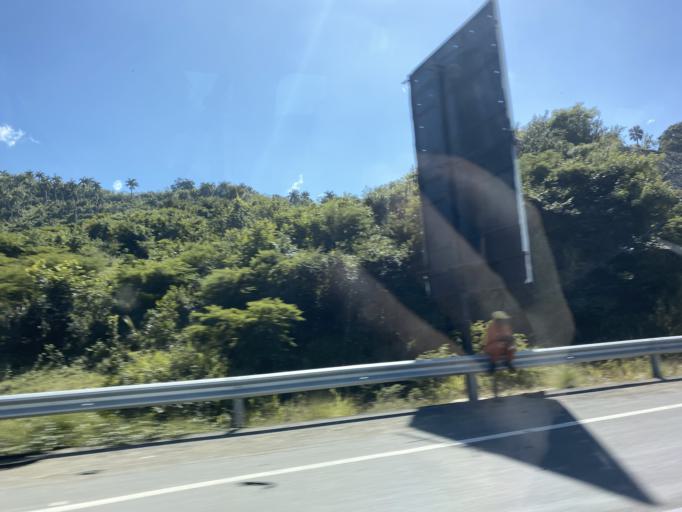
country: DO
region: Puerto Plata
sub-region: Puerto Plata
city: Puerto Plata
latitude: 19.8259
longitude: -70.7728
